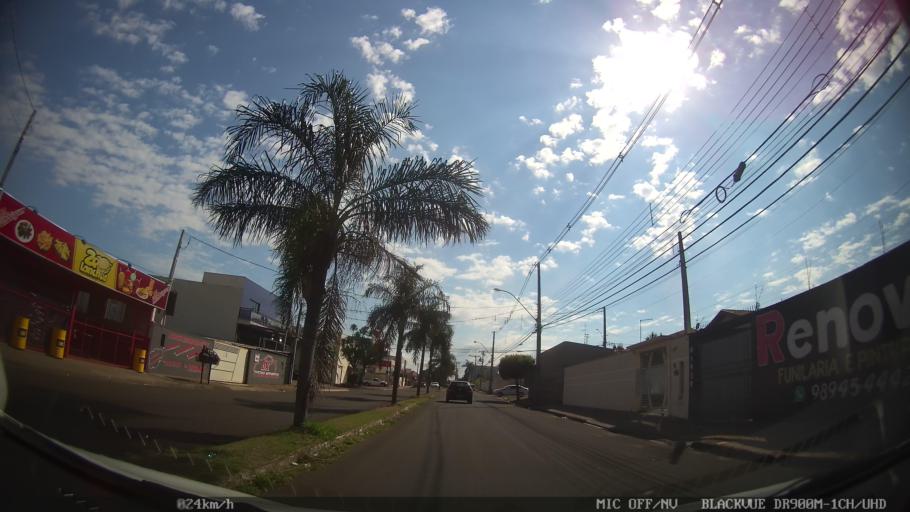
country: BR
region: Sao Paulo
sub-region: Americana
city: Americana
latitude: -22.7384
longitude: -47.3031
